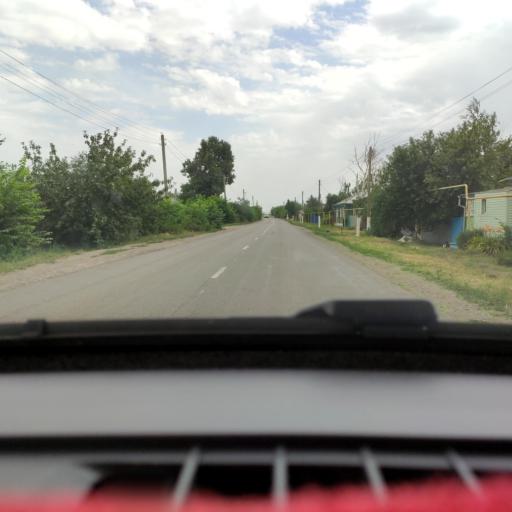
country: RU
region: Voronezj
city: Davydovka
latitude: 51.2187
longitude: 39.5260
